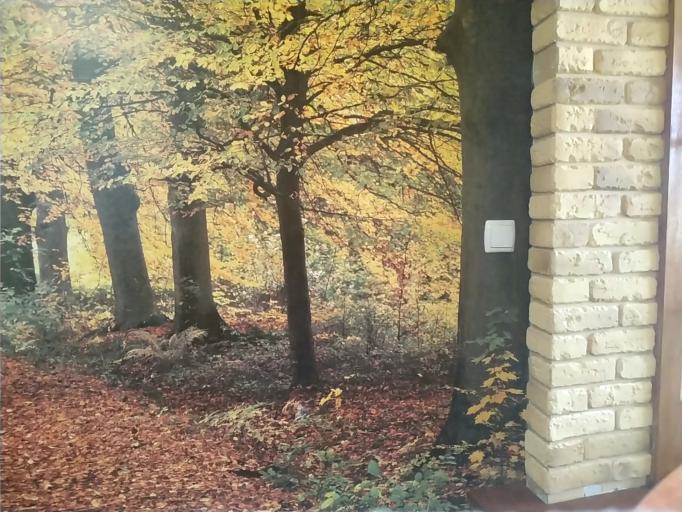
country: RU
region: Tverskaya
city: Vyshniy Volochek
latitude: 57.6615
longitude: 34.5394
